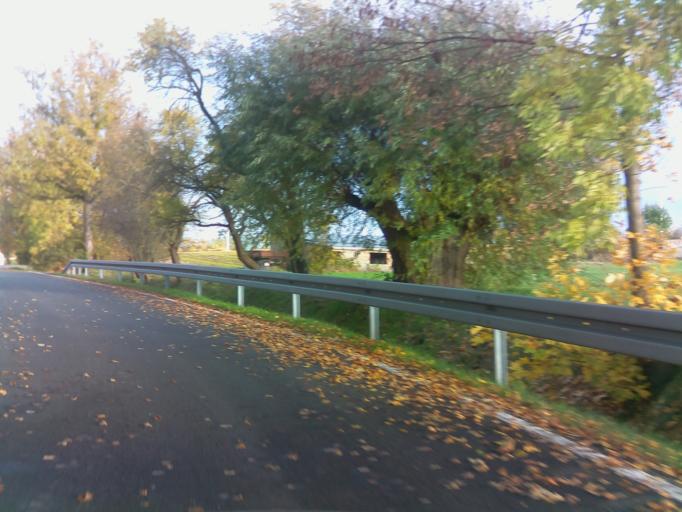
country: DE
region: Thuringia
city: Blankenhain
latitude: 50.8426
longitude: 11.3536
